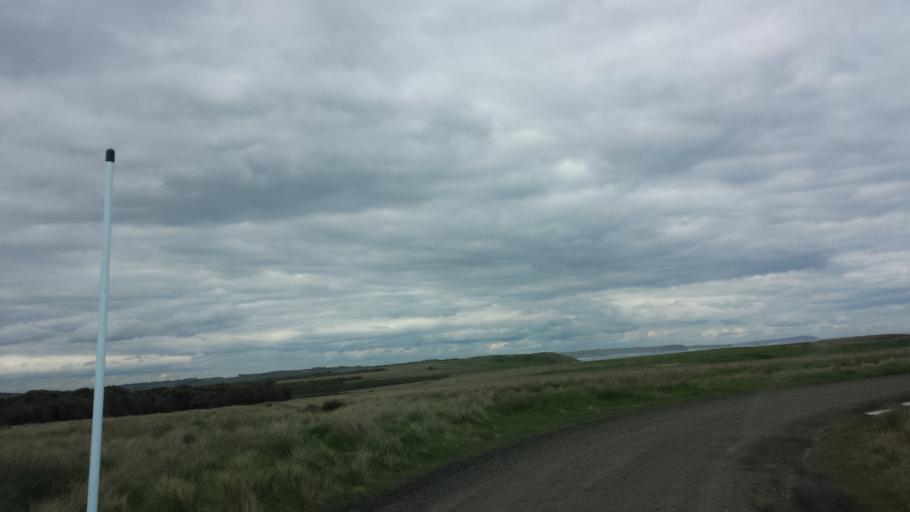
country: AU
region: Victoria
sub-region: Bass Coast
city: Phillip Island
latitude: -38.5151
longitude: 145.1294
